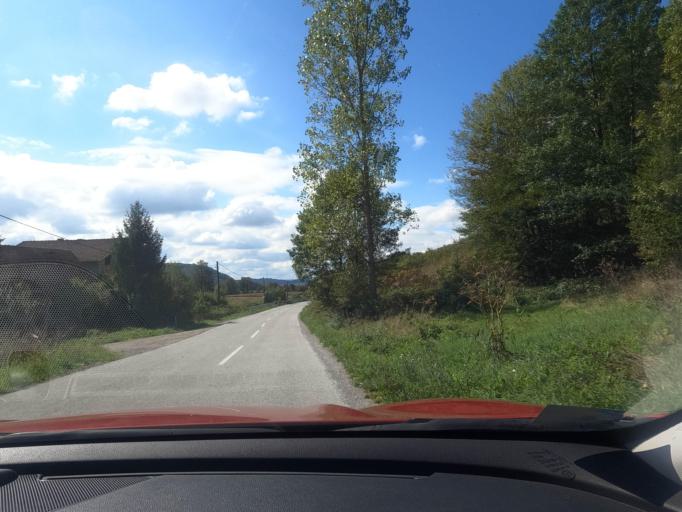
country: BA
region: Federation of Bosnia and Herzegovina
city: Velika Kladusa
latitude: 45.2200
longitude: 15.8311
